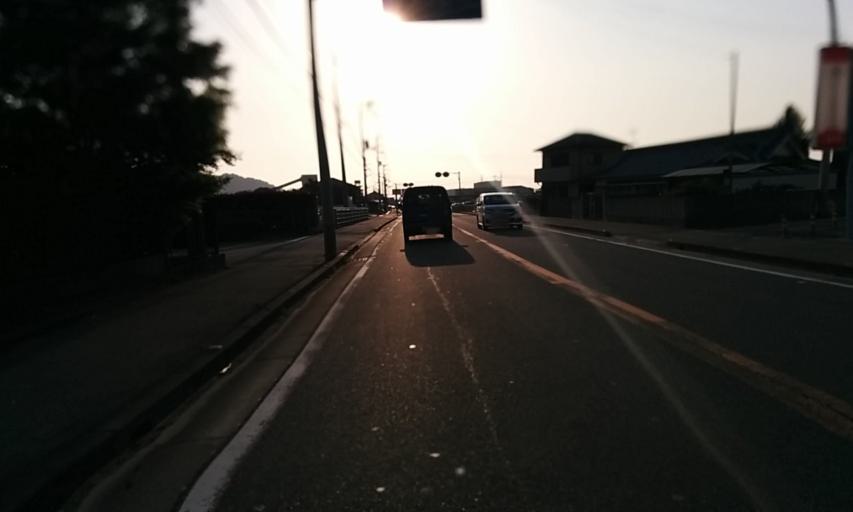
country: JP
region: Ehime
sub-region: Shikoku-chuo Shi
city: Matsuyama
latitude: 33.7824
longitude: 132.8059
